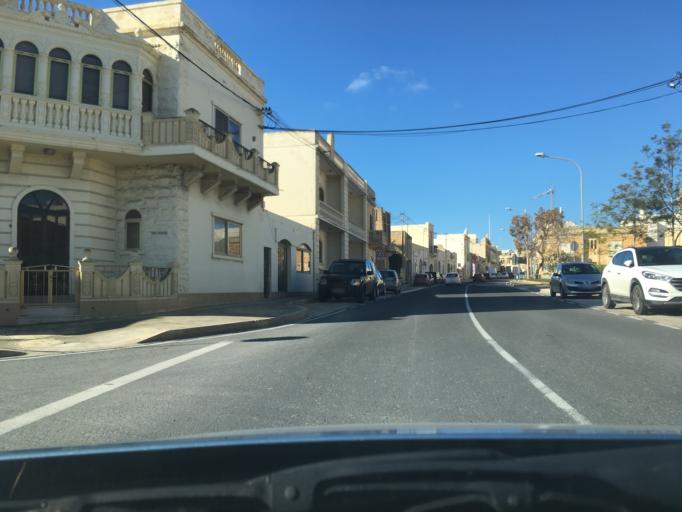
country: MT
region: Ghajnsielem
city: Ghajnsielem
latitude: 36.0242
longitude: 14.2879
